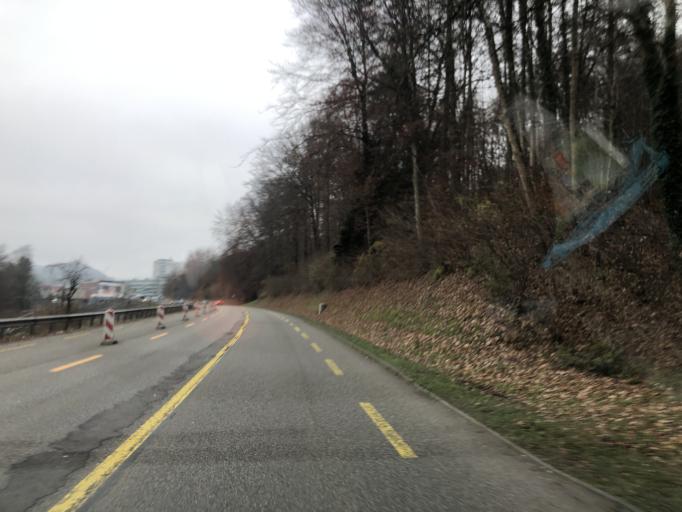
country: CH
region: Aargau
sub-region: Bezirk Baden
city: Turgi
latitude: 47.4823
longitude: 8.2737
